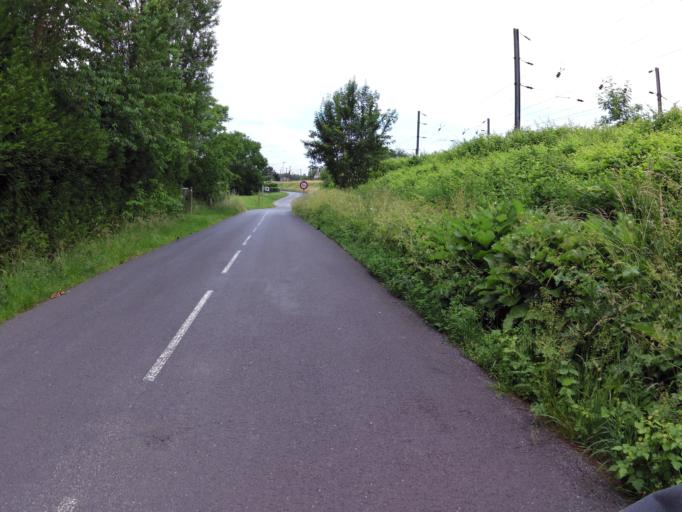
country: FR
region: Champagne-Ardenne
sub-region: Departement des Ardennes
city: Lumes
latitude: 49.7325
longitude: 4.7833
